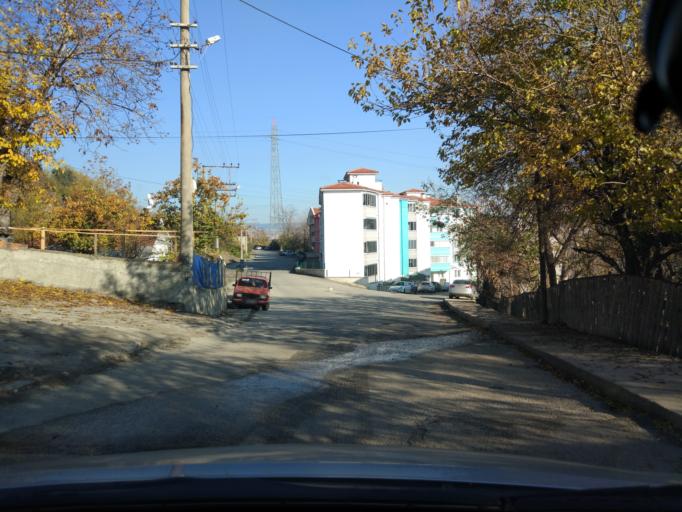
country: TR
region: Karabuk
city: Karabuk
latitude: 41.2055
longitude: 32.6300
